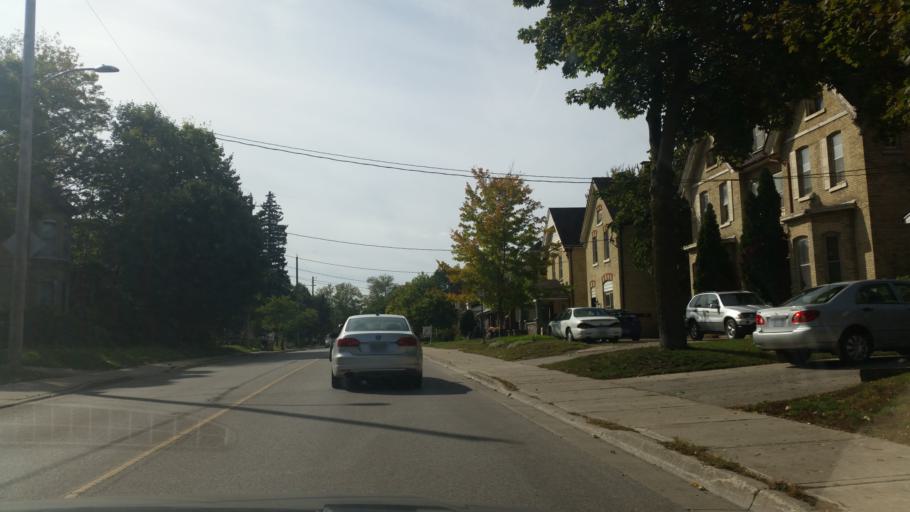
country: CA
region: Ontario
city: London
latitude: 42.9786
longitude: -81.2586
